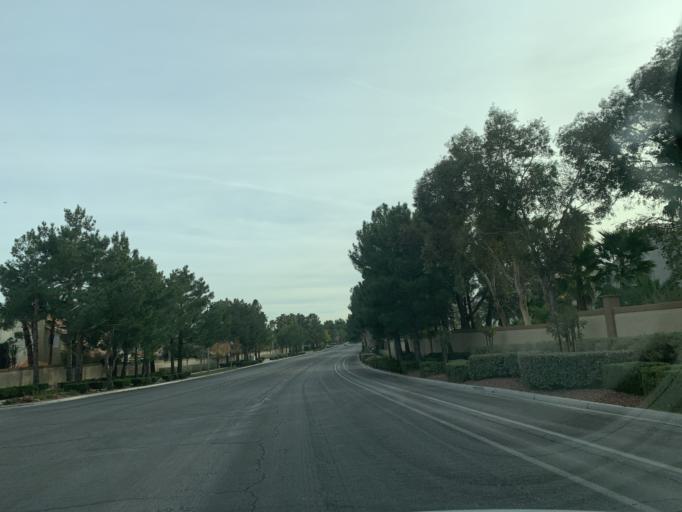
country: US
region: Nevada
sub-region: Clark County
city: Summerlin South
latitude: 36.1488
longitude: -115.3070
